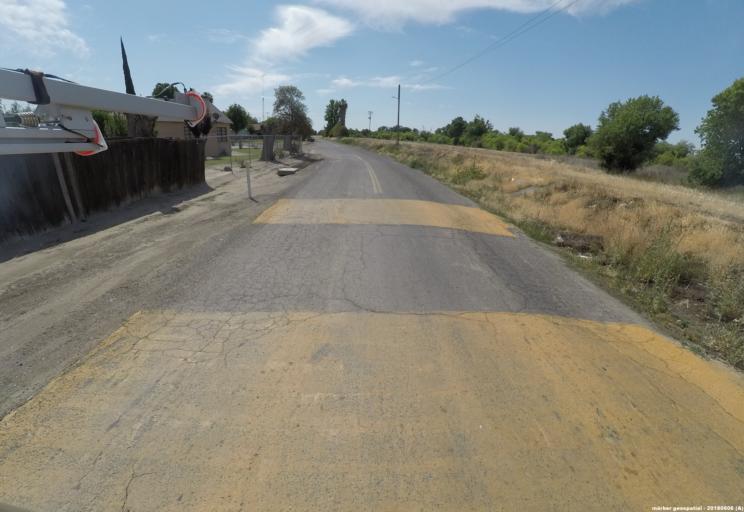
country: US
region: California
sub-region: Fresno County
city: Firebaugh
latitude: 36.8575
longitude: -120.4417
